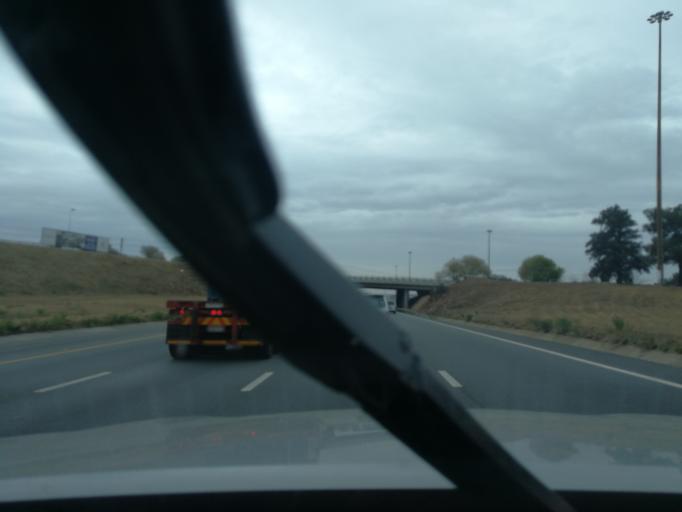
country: ZA
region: Gauteng
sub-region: Ekurhuleni Metropolitan Municipality
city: Germiston
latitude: -26.2389
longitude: 28.1274
